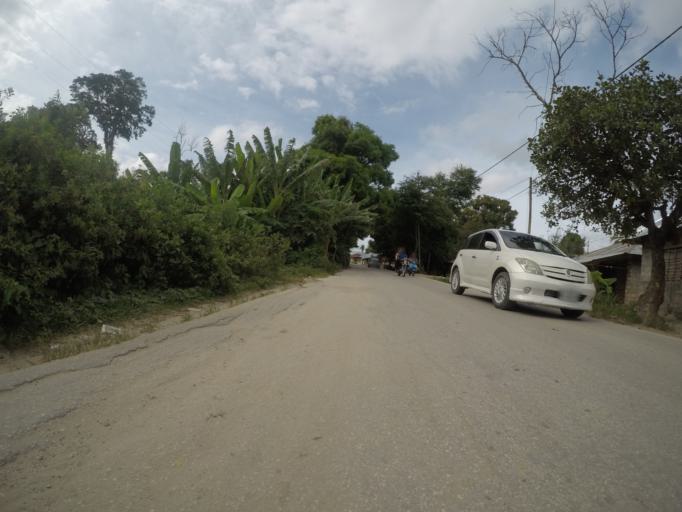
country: TZ
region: Pemba South
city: Chake Chake
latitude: -5.2425
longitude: 39.7823
